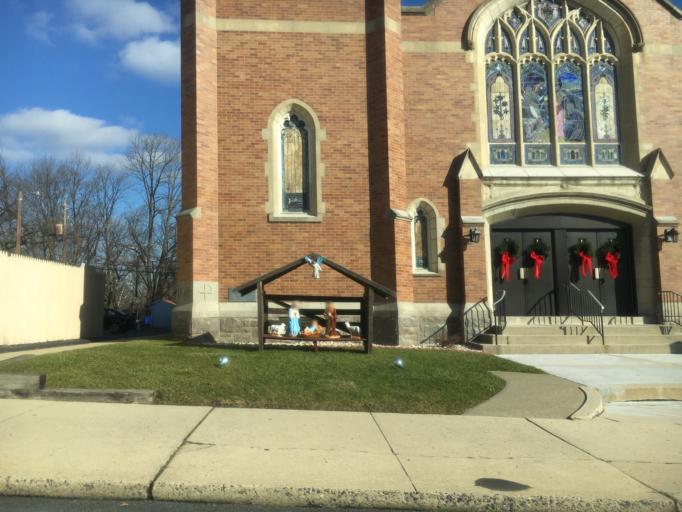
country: US
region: Pennsylvania
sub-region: Northampton County
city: Northampton
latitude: 40.6803
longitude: -75.4909
